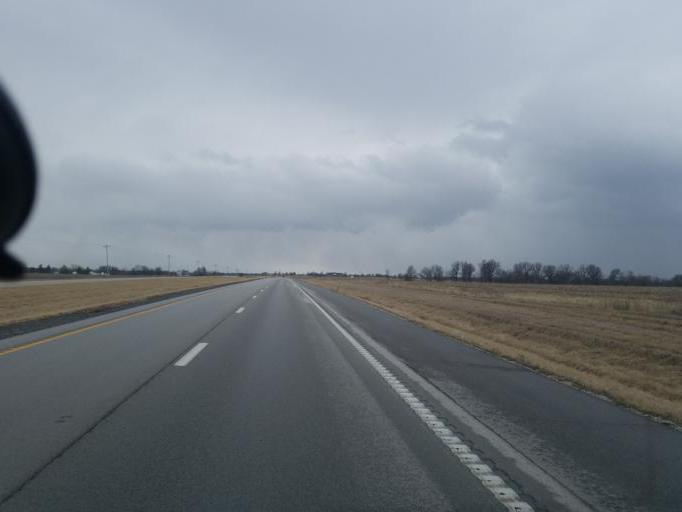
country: US
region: Missouri
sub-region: Macon County
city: Macon
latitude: 39.8099
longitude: -92.4745
